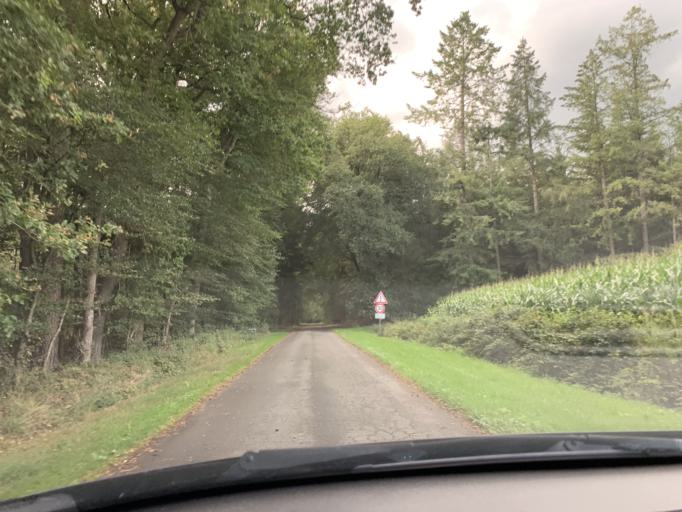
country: DE
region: Lower Saxony
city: Westerstede
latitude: 53.2637
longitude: 8.0076
